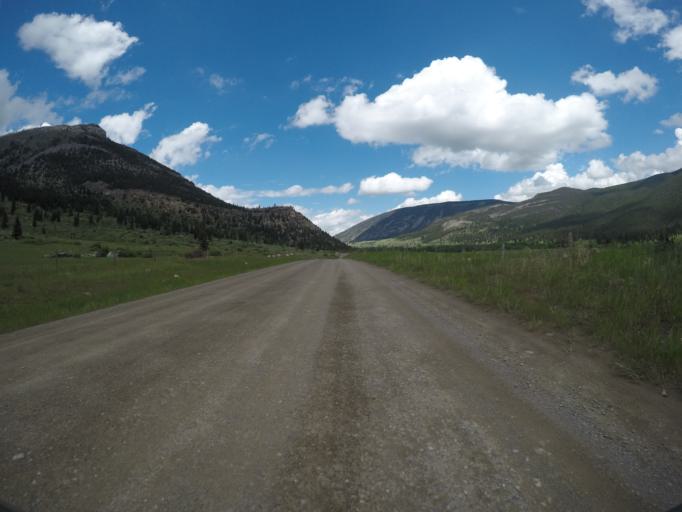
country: US
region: Montana
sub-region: Park County
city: Livingston
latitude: 45.5253
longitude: -110.2206
